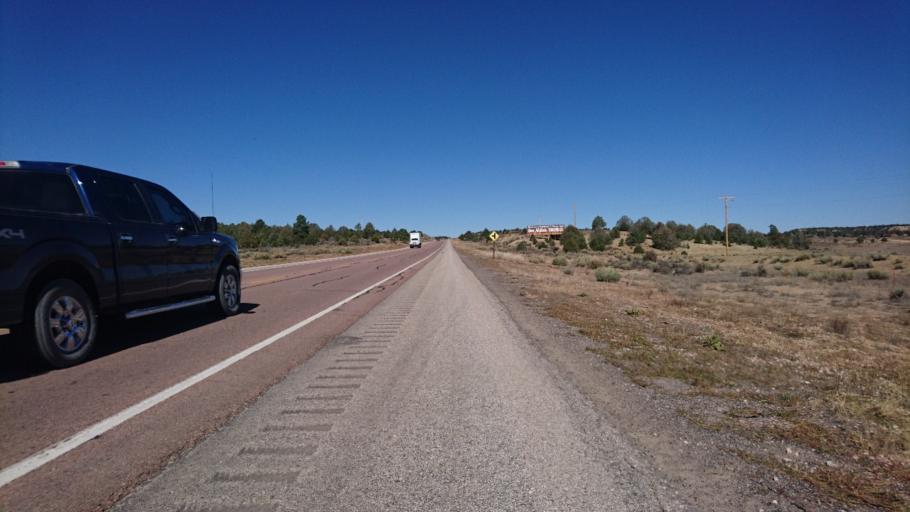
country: US
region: New Mexico
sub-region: McKinley County
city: Black Rock
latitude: 35.2929
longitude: -108.7565
